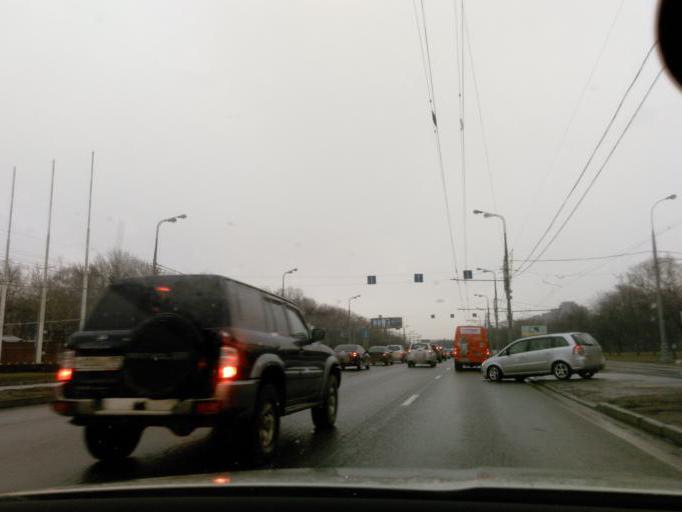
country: RU
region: Moscow
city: Pokrovskoye-Streshnevo
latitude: 55.8143
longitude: 37.4699
